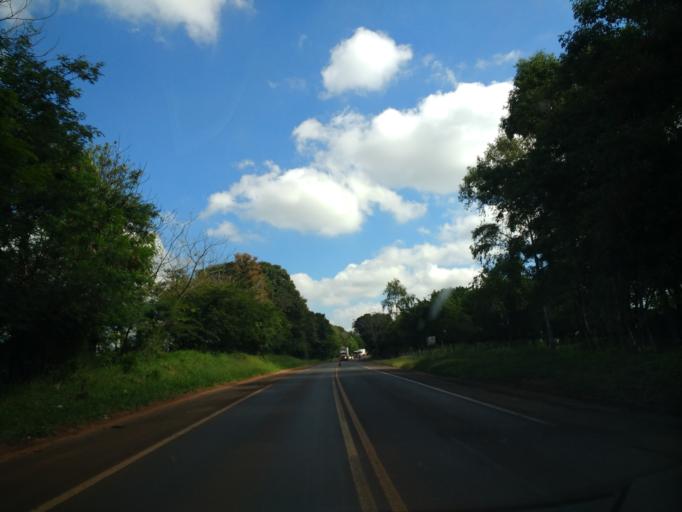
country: BR
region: Parana
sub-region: Umuarama
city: Umuarama
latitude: -23.8854
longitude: -53.4005
